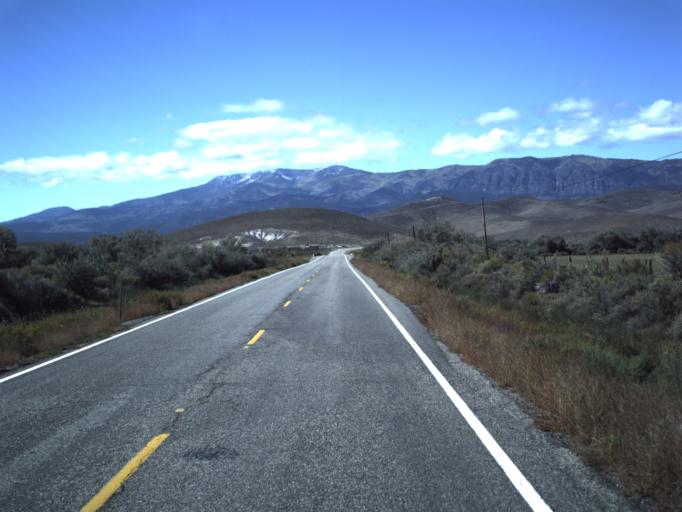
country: US
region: Utah
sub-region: Piute County
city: Junction
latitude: 38.2084
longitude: -112.2035
